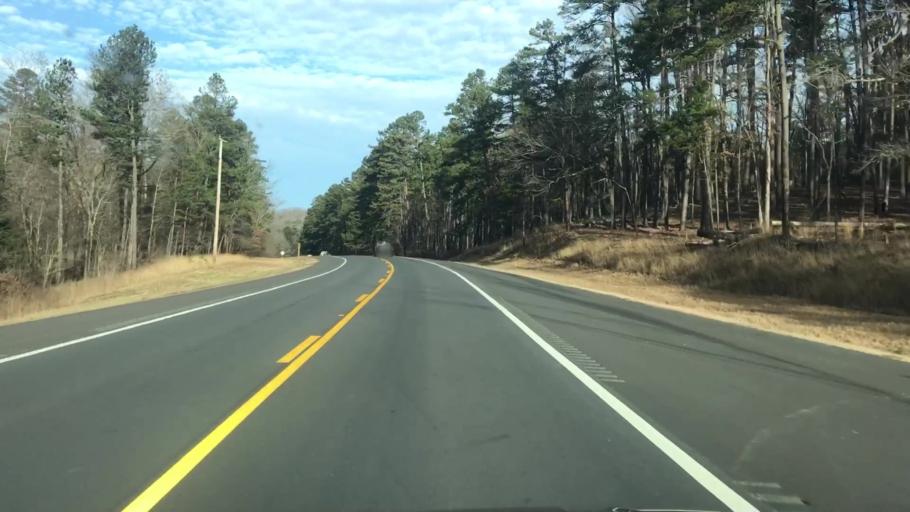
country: US
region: Arkansas
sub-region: Pike County
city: Glenwood
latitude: 34.5163
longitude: -93.3843
